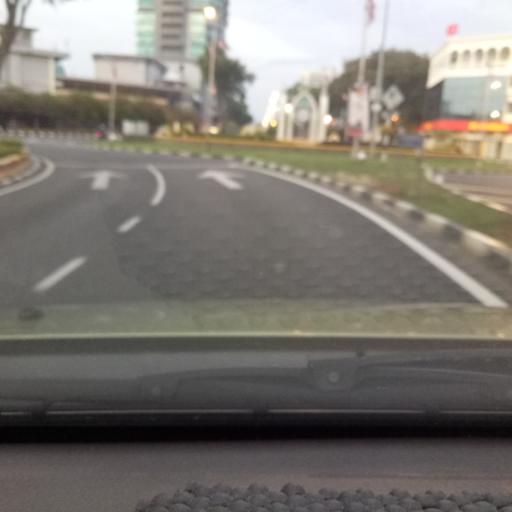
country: MY
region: Kedah
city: Alor Setar
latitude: 6.1195
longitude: 100.3689
